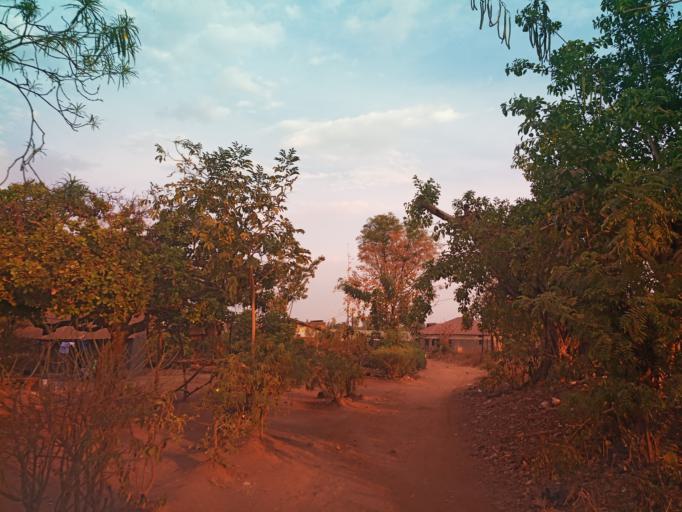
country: UG
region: Northern Region
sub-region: Arua District
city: Arua
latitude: 3.0345
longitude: 30.9201
